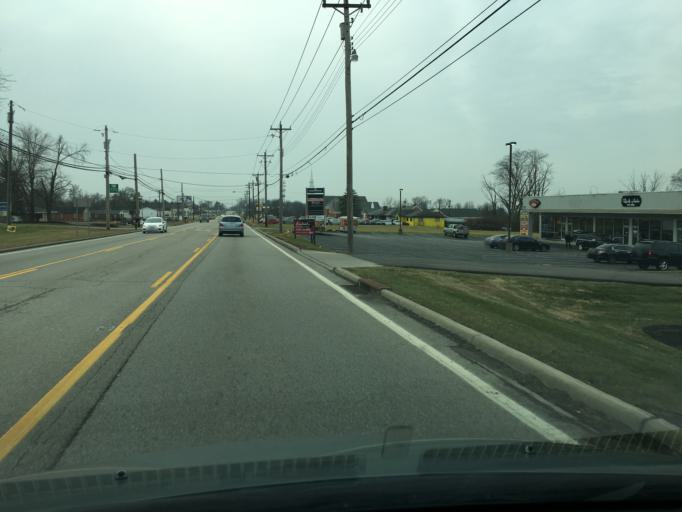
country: US
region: Ohio
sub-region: Hamilton County
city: Highpoint
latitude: 39.3154
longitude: -84.3735
